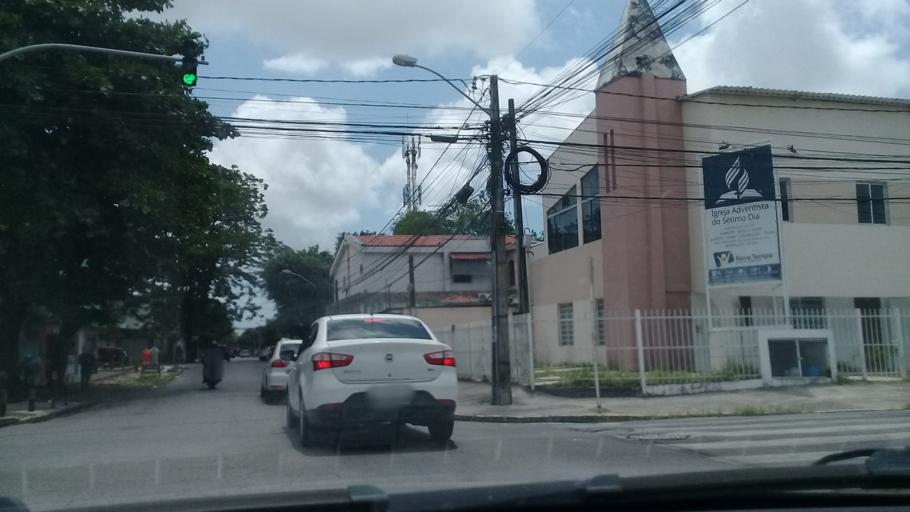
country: BR
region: Pernambuco
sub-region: Recife
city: Recife
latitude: -8.1078
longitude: -34.9258
